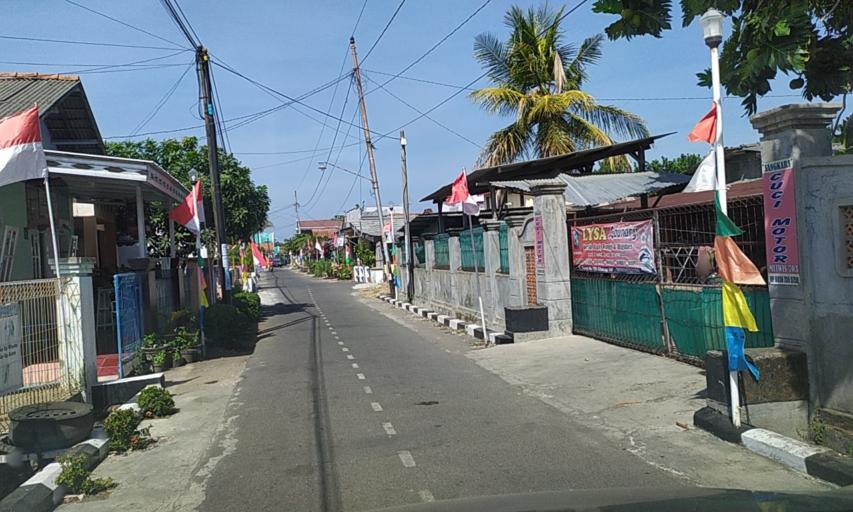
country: ID
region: Central Java
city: Karangbadar Kidul
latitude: -7.7147
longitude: 109.0064
